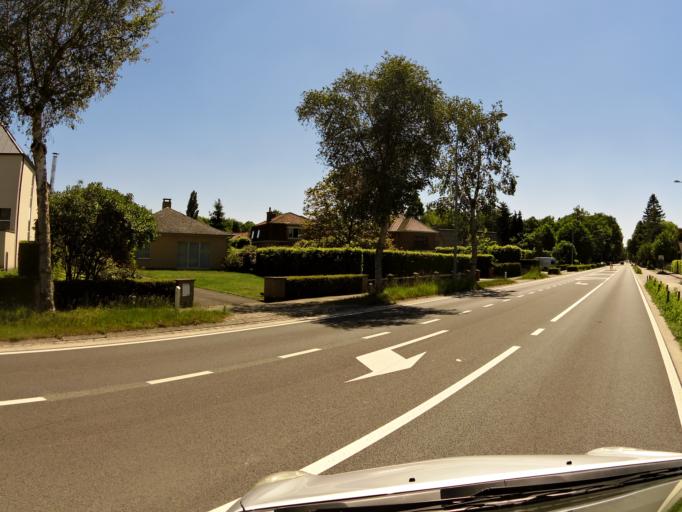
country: BE
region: Flanders
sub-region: Provincie West-Vlaanderen
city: Brugge
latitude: 51.1854
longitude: 3.1900
